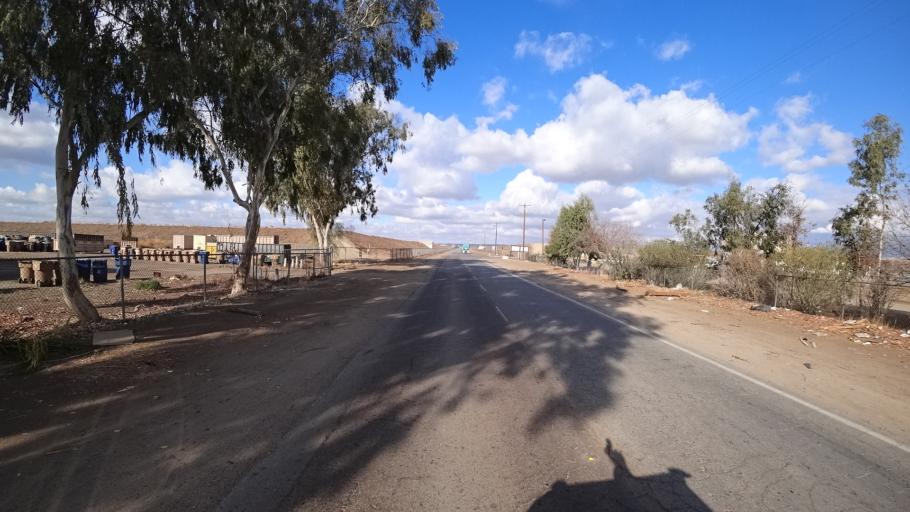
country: US
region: California
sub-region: Kern County
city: Greenfield
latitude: 35.3267
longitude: -118.9677
